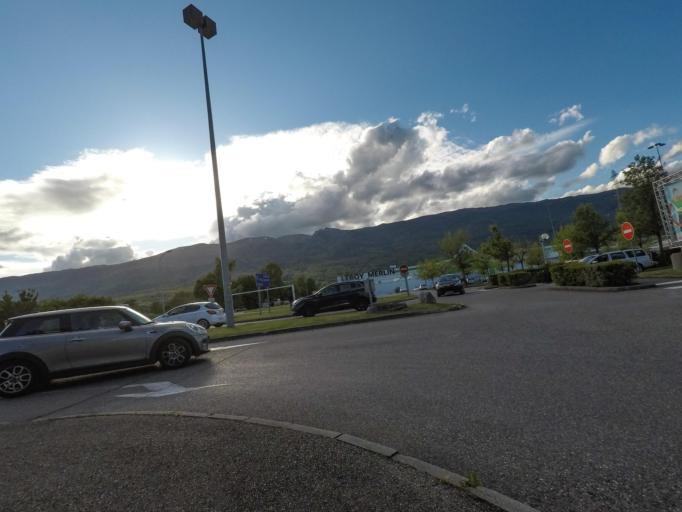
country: FR
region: Rhone-Alpes
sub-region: Departement de l'Ain
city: Thoiry
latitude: 46.2274
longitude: 5.9922
